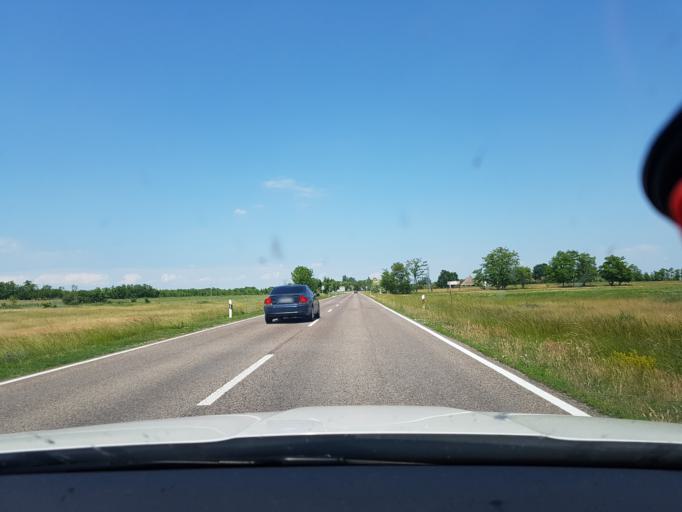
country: HU
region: Hajdu-Bihar
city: Egyek
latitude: 47.5862
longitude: 20.8533
